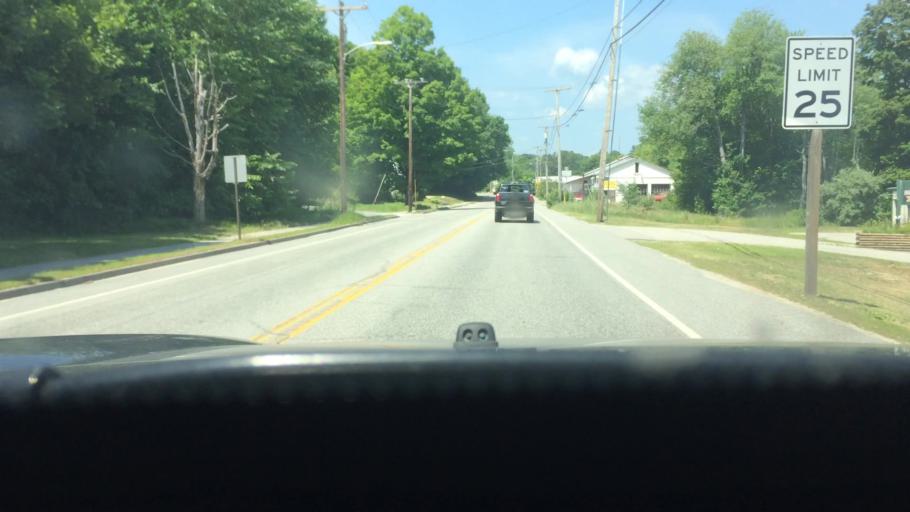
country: US
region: Maine
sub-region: Androscoggin County
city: Mechanic Falls
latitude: 44.1105
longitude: -70.3852
